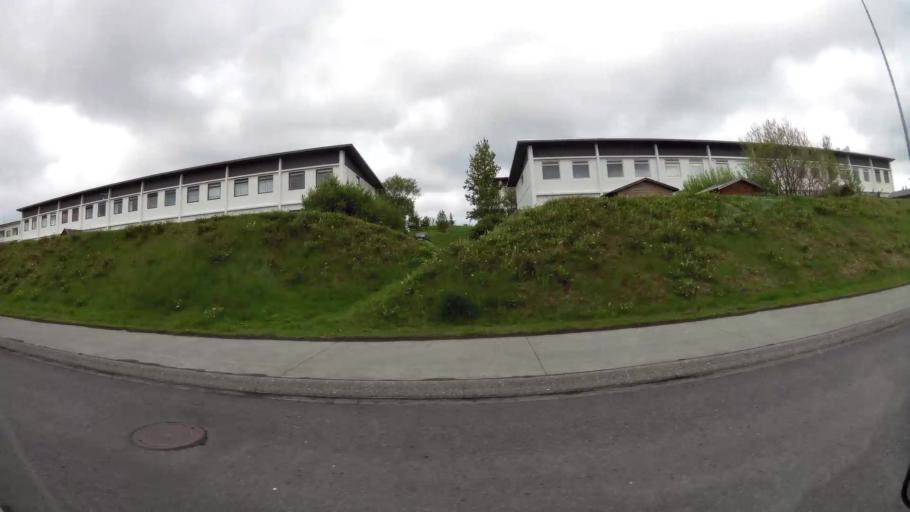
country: IS
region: Capital Region
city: Reykjavik
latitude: 64.1210
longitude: -21.8620
